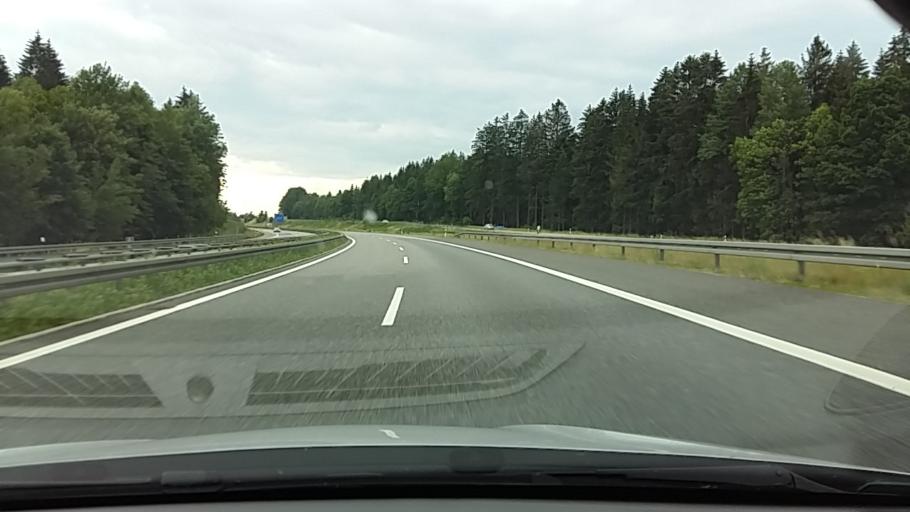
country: DE
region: Bavaria
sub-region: Upper Palatinate
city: Vohenstrauss
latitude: 49.6184
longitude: 12.3701
